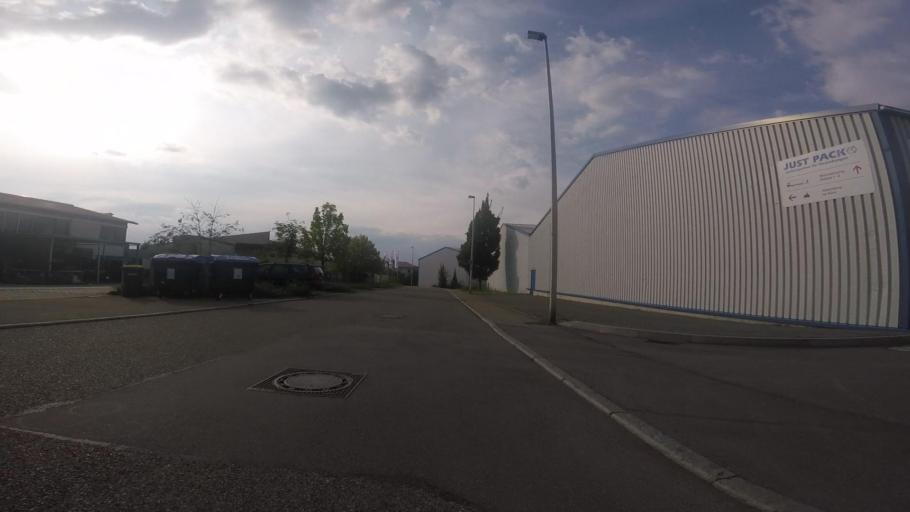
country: DE
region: Baden-Wuerttemberg
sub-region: Regierungsbezirk Stuttgart
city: Aspach
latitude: 48.9736
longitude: 9.3871
